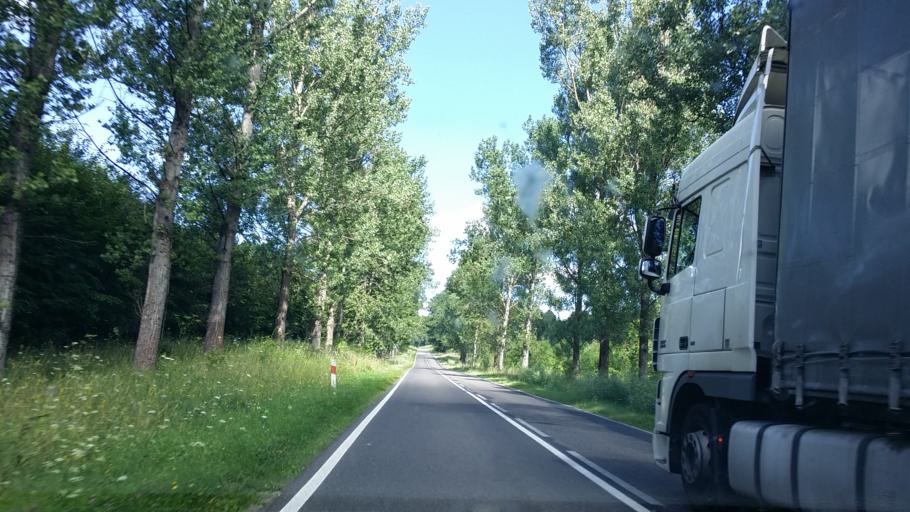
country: PL
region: West Pomeranian Voivodeship
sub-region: Powiat drawski
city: Kalisz Pomorski
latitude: 53.3729
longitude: 15.8712
